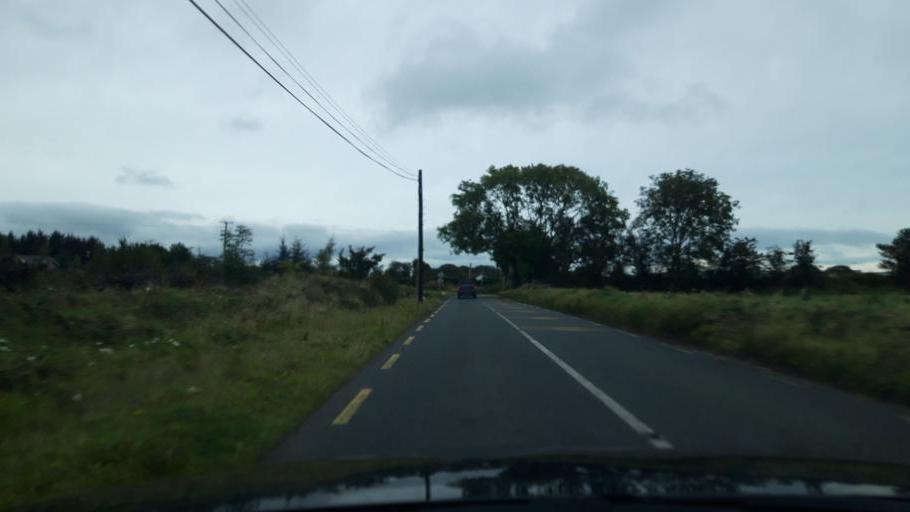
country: IE
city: Newtownmountkennedy
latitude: 53.0990
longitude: -6.2007
